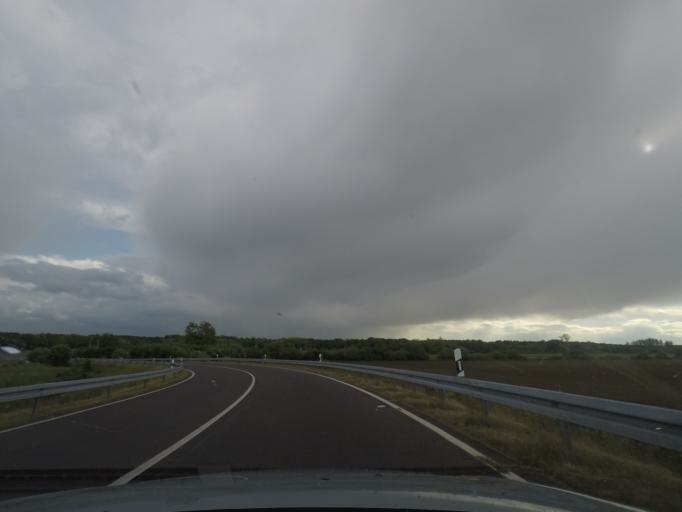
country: DE
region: Lower Saxony
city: Grafhorst
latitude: 52.4347
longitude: 10.9461
